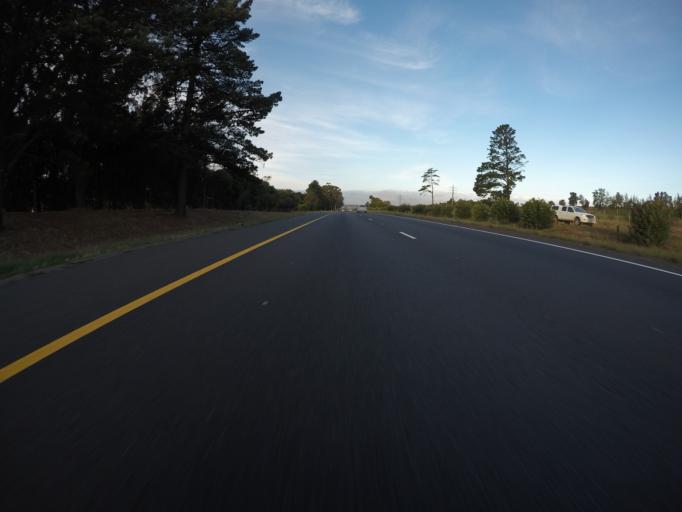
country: ZA
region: Western Cape
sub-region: City of Cape Town
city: Kraaifontein
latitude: -33.8071
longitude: 18.8369
